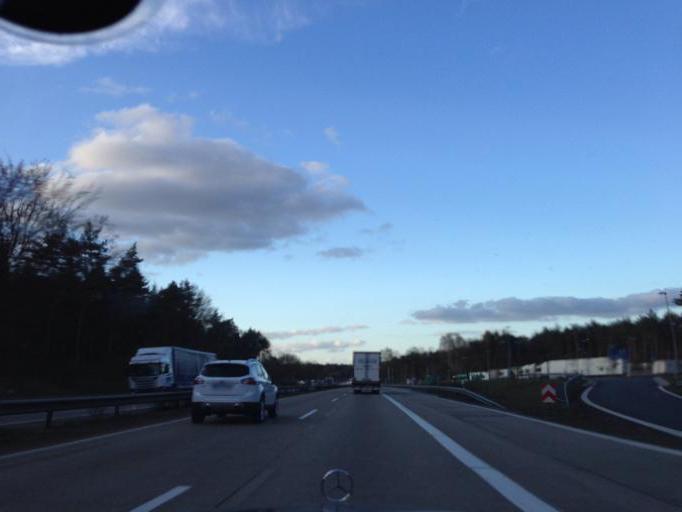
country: DE
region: Lower Saxony
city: Bad Fallingbostel
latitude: 52.8073
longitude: 9.6790
